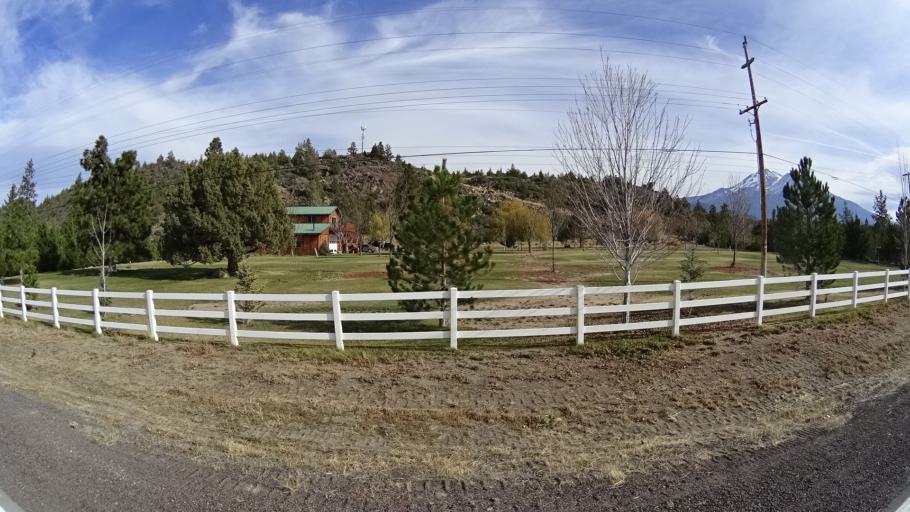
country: US
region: California
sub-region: Siskiyou County
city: Weed
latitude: 41.5083
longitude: -122.3641
